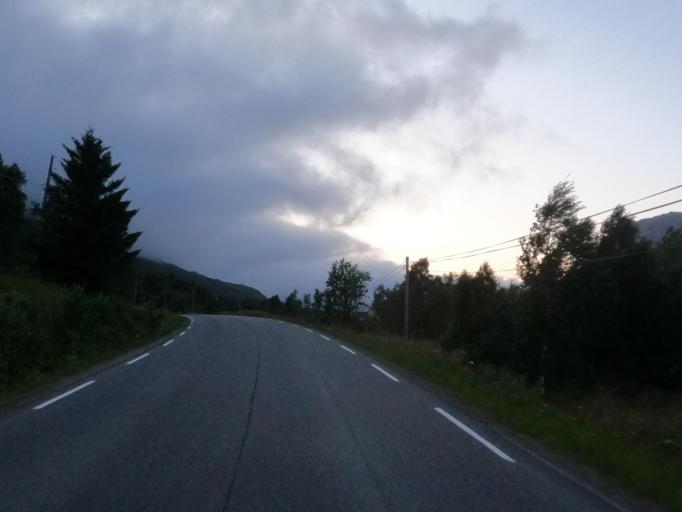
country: NO
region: Nordland
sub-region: Lodingen
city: Lodingen
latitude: 68.5754
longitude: 15.7948
